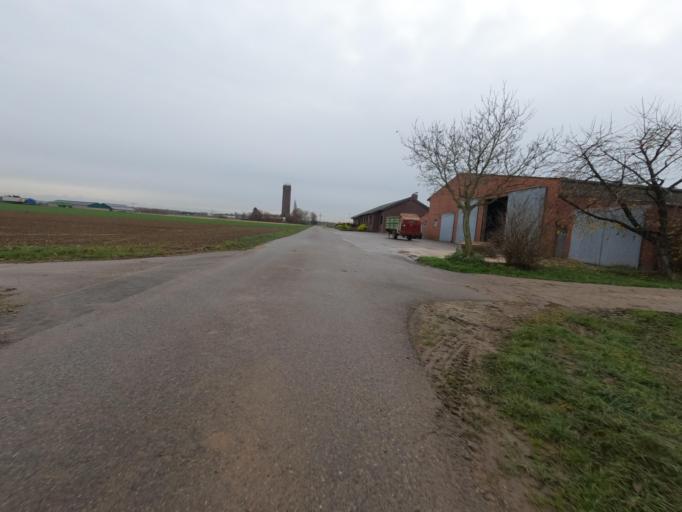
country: DE
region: North Rhine-Westphalia
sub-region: Regierungsbezirk Koln
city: Heinsberg
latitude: 51.0443
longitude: 6.1266
